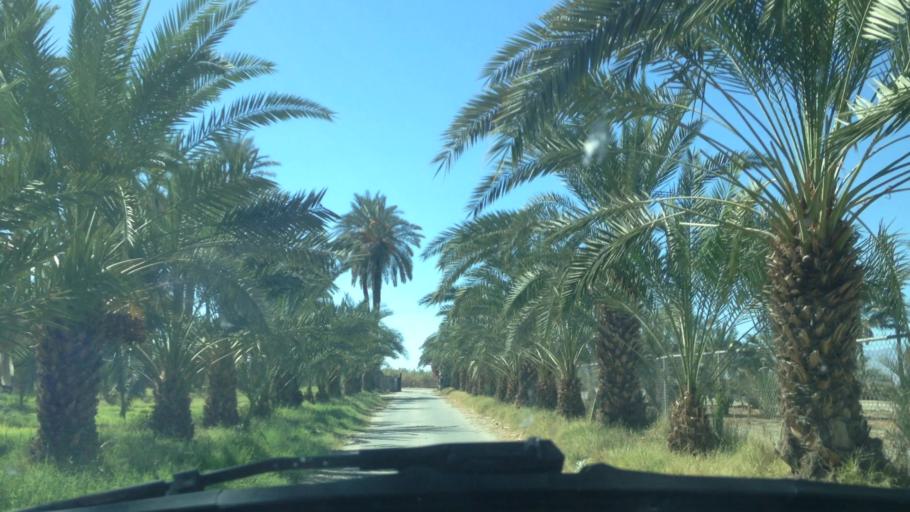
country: US
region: California
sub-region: Riverside County
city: Mecca
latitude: 33.5422
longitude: -116.0307
